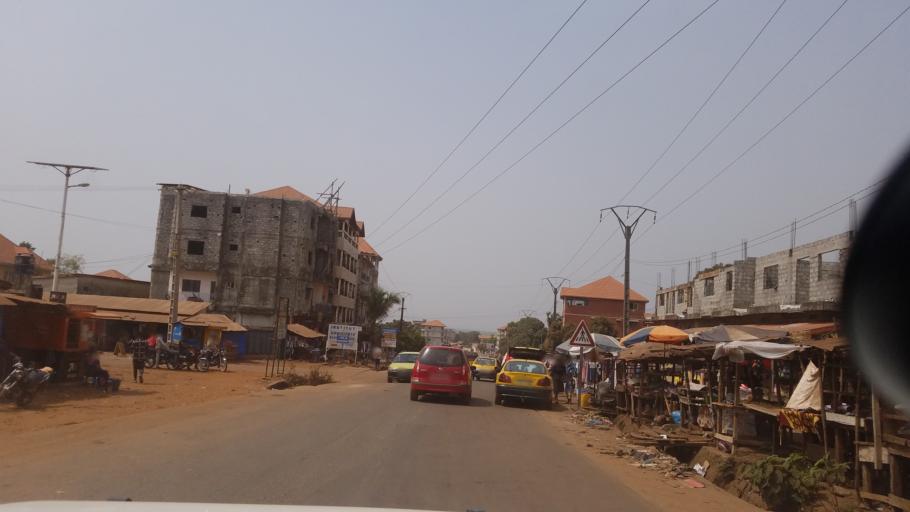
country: GN
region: Kindia
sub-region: Prefecture de Dubreka
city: Dubreka
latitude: 9.6759
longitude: -13.5657
